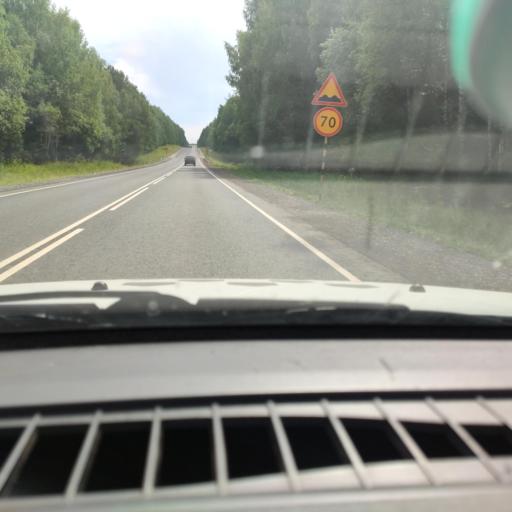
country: RU
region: Perm
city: Zyukayka
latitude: 58.2961
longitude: 54.7778
